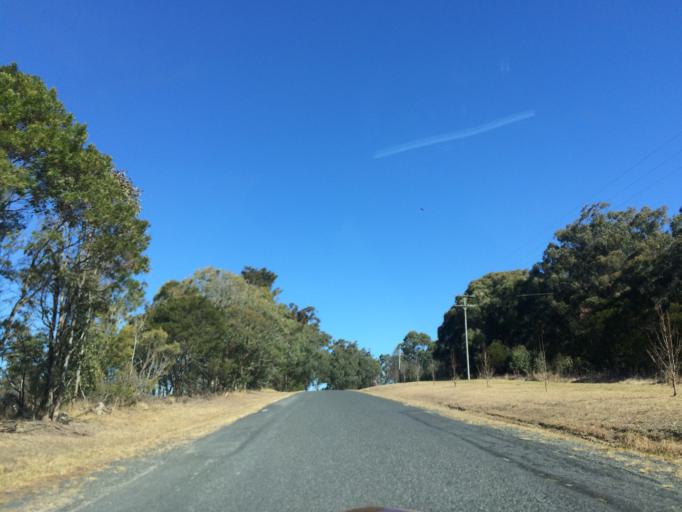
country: AU
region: Queensland
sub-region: Southern Downs
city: Stanthorpe
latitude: -28.6495
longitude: 152.0844
